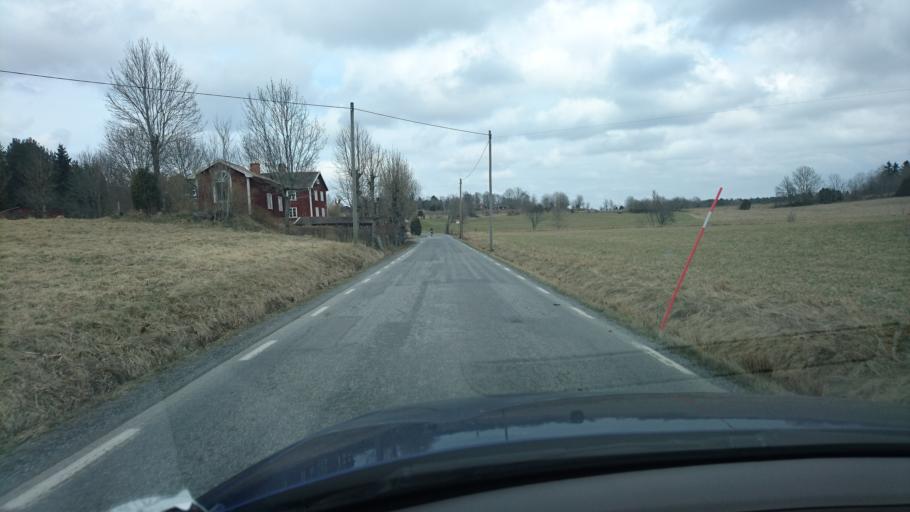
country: SE
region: Stockholm
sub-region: Norrtalje Kommun
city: Bjorko
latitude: 59.8024
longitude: 18.9564
